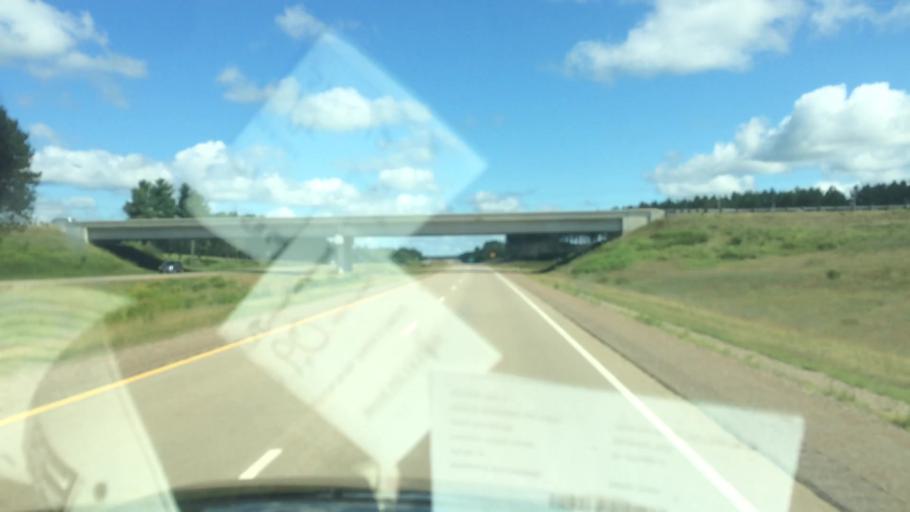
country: US
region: Wisconsin
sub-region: Lincoln County
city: Tomahawk
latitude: 45.4696
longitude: -89.6910
